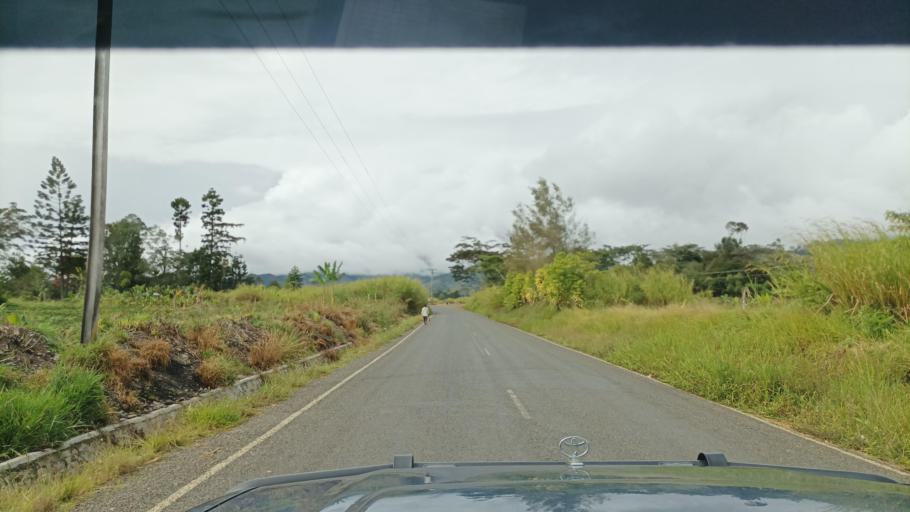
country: PG
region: Jiwaka
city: Minj
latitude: -5.8947
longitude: 144.6824
